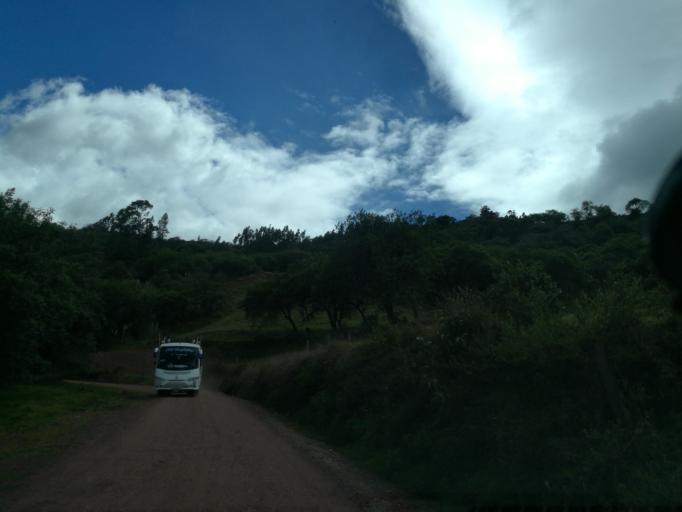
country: CO
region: Boyaca
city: Socota
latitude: 6.1089
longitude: -72.7175
